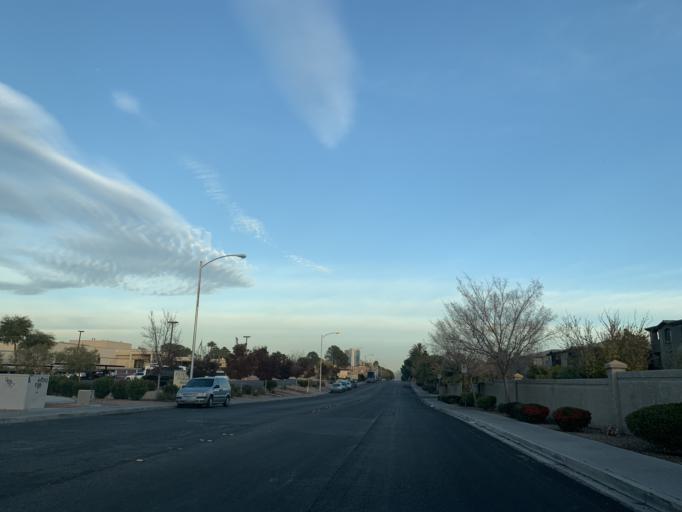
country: US
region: Nevada
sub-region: Clark County
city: Spring Valley
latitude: 36.1108
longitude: -115.2238
